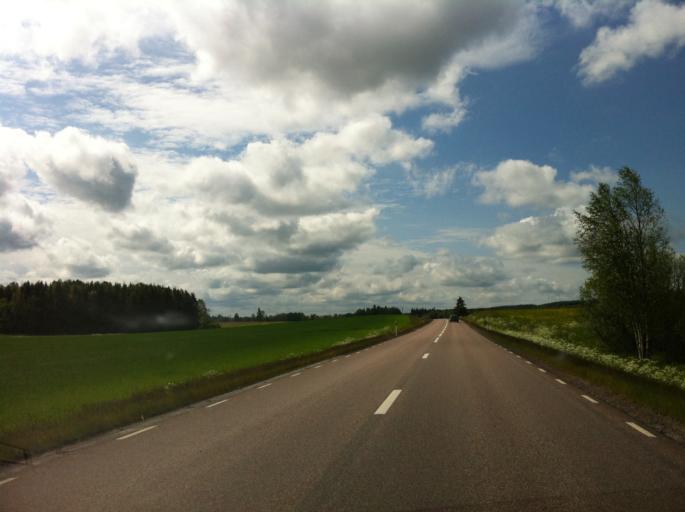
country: SE
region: Vaermland
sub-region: Sunne Kommun
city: Sunne
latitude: 59.6562
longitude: 13.1537
